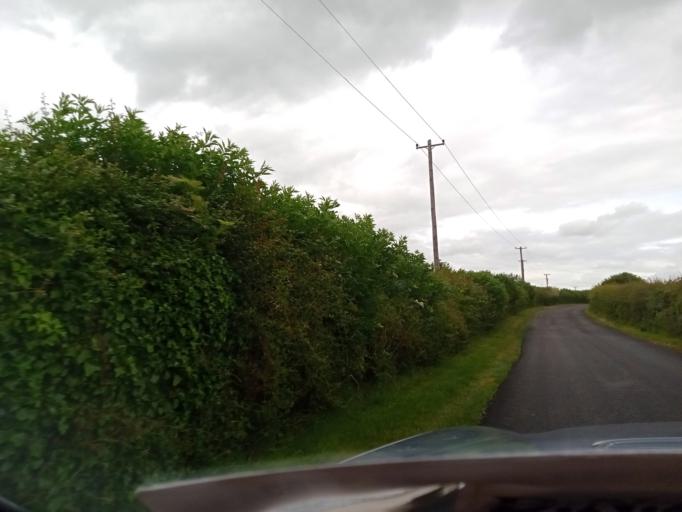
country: IE
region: Leinster
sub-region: Kilkenny
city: Thomastown
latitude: 52.5544
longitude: -7.2116
